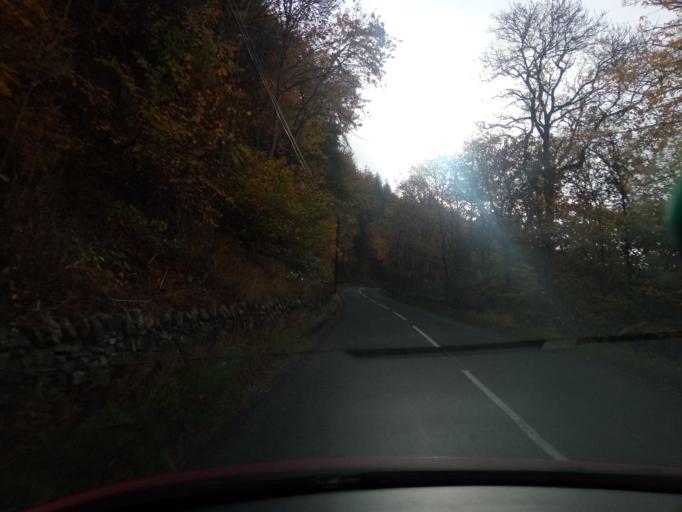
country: GB
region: Scotland
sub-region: The Scottish Borders
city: Selkirk
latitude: 55.6004
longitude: -2.8680
